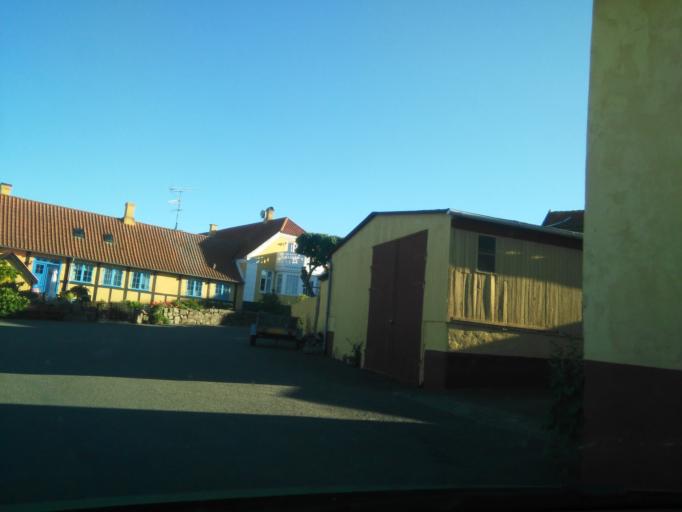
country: DK
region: Capital Region
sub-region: Bornholm Kommune
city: Ronne
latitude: 55.2764
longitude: 14.8046
